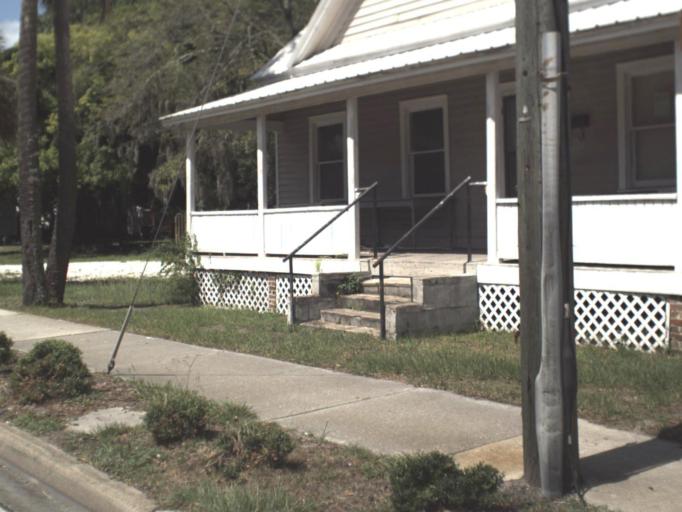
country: US
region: Florida
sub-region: Nassau County
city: Fernandina Beach
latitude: 30.6694
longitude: -81.4590
